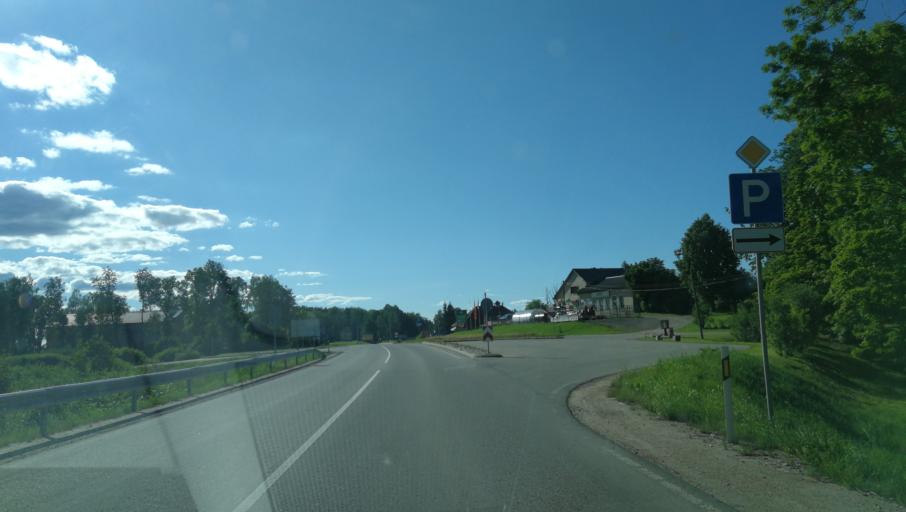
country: LV
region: Vecpiebalga
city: Vecpiebalga
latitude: 57.0576
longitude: 25.8260
